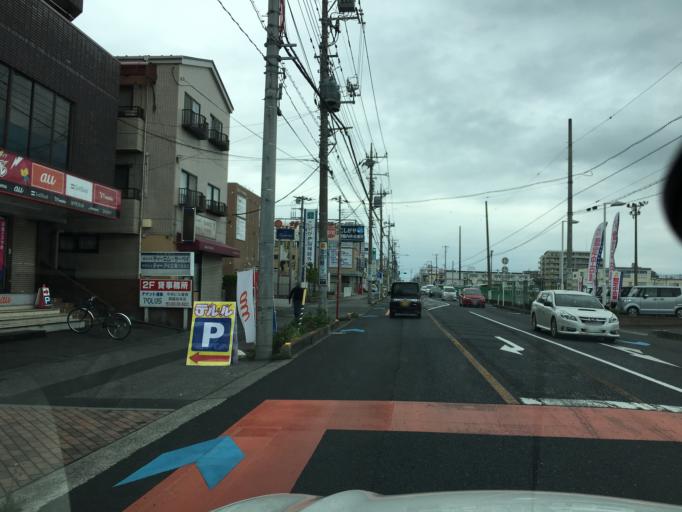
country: JP
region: Saitama
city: Koshigaya
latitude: 35.8672
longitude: 139.7947
